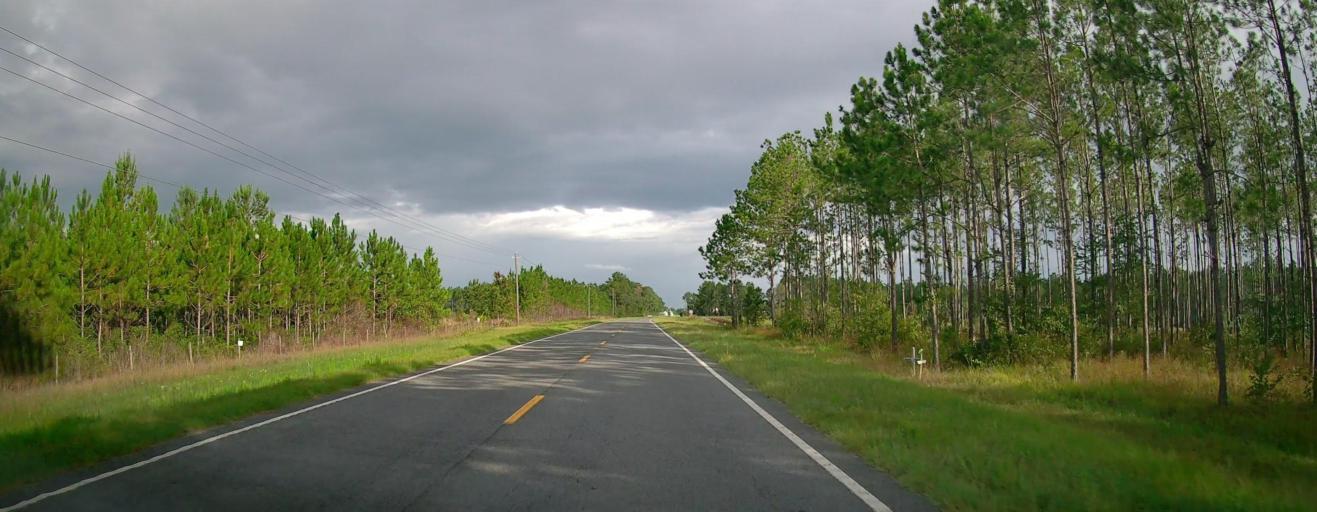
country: US
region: Georgia
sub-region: Coffee County
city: Nicholls
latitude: 31.3596
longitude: -82.6226
